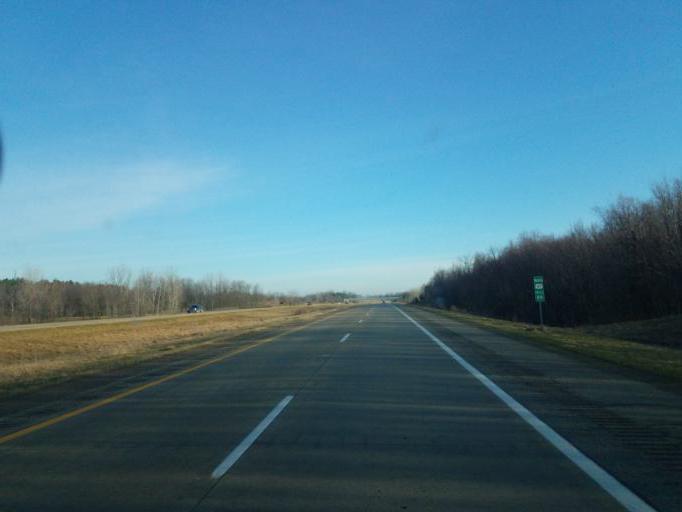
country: US
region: Michigan
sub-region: Clinton County
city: DeWitt
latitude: 42.8995
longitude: -84.5174
